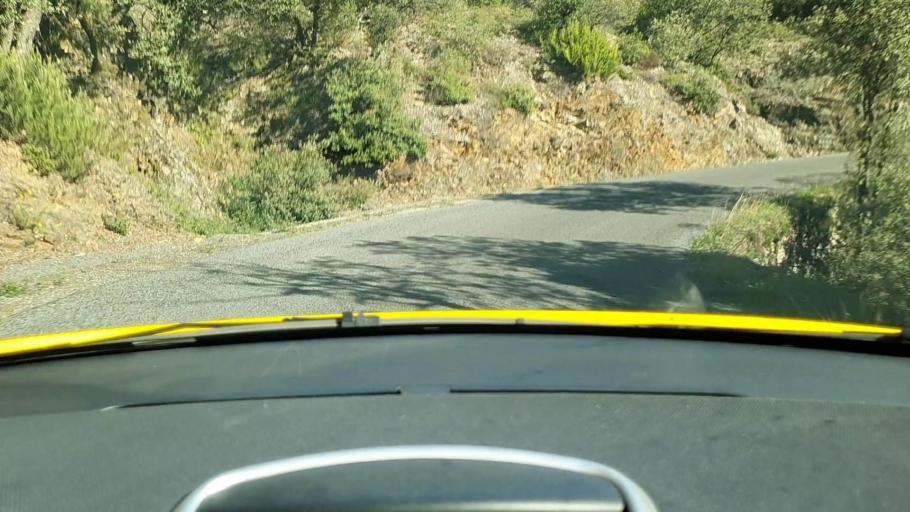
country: FR
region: Languedoc-Roussillon
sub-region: Departement du Gard
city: Sumene
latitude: 44.0329
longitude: 3.6975
